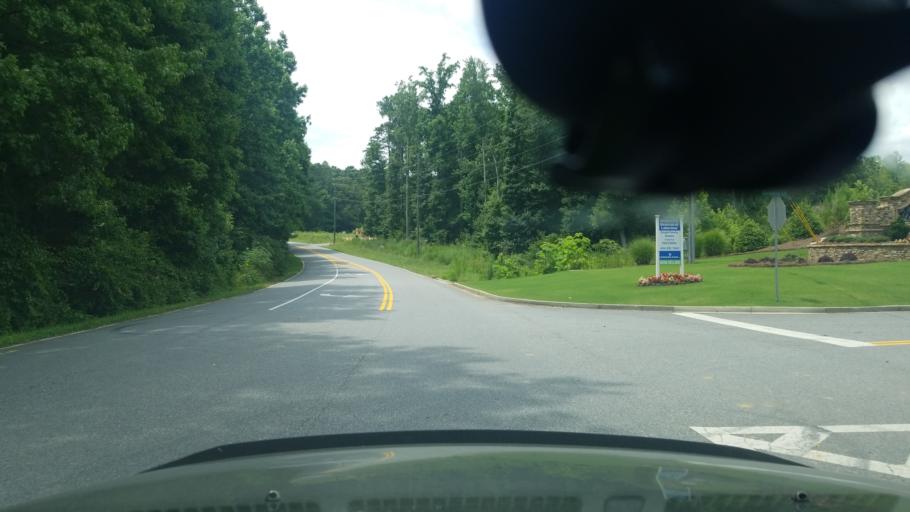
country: US
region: Georgia
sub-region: Forsyth County
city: Cumming
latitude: 34.2207
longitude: -84.2059
